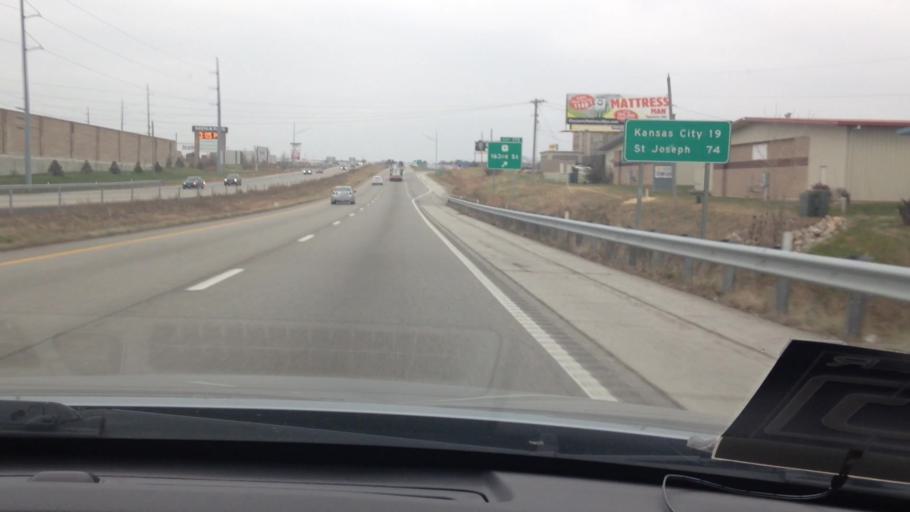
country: US
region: Missouri
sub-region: Cass County
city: Belton
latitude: 38.8217
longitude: -94.5152
